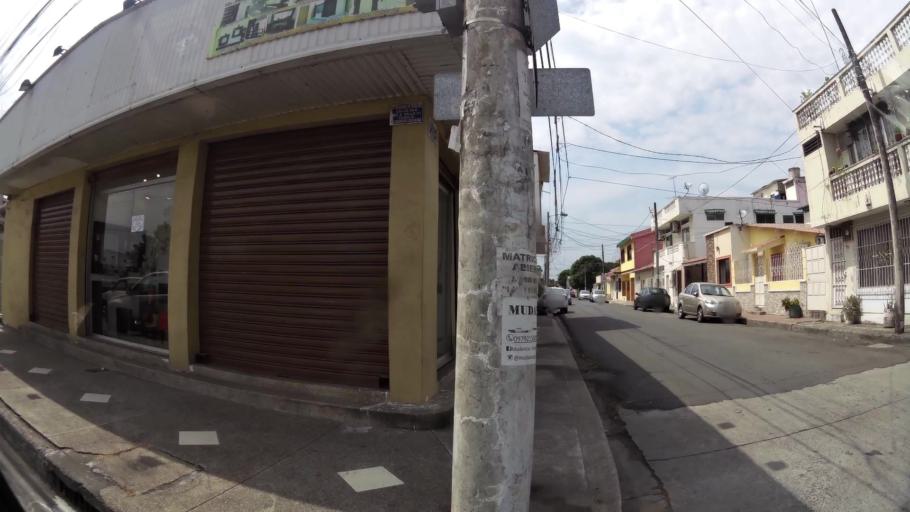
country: EC
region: Guayas
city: Eloy Alfaro
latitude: -2.1454
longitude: -79.9007
